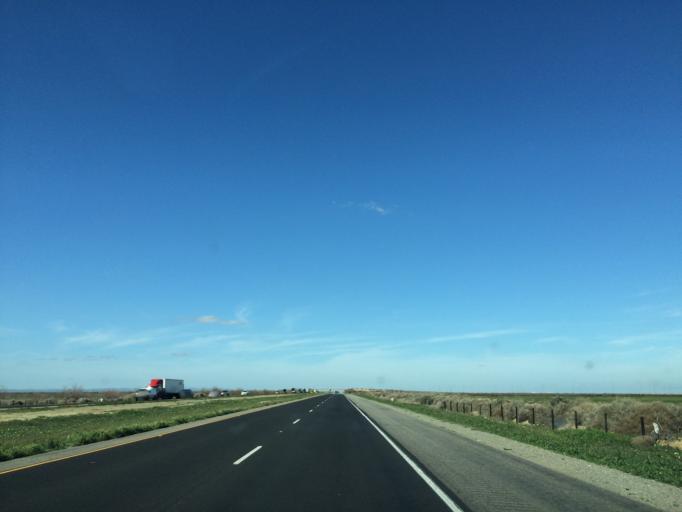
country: US
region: California
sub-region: Kern County
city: Lost Hills
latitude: 35.7804
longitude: -119.7753
